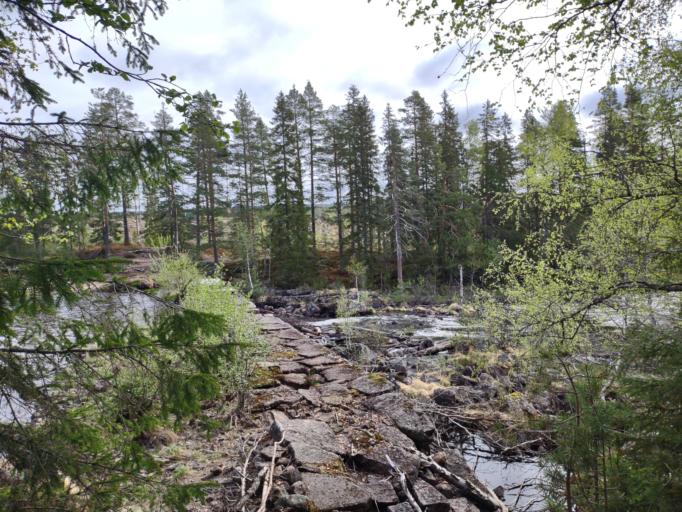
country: NO
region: Oppland
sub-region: Lunner
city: Grua
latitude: 60.2872
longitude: 10.7753
